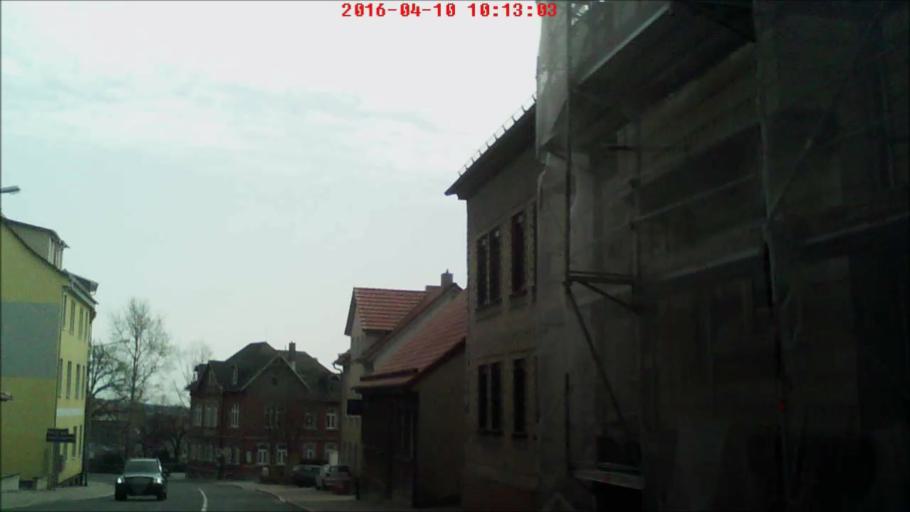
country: DE
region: Thuringia
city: Ilmenau
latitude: 50.6883
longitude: 10.9090
